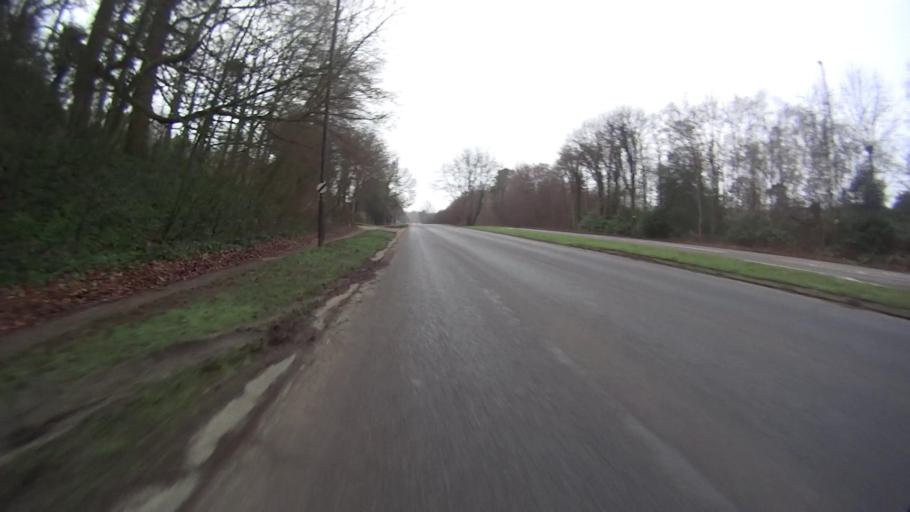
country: GB
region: England
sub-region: West Sussex
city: Broadfield
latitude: 51.0963
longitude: -0.1937
